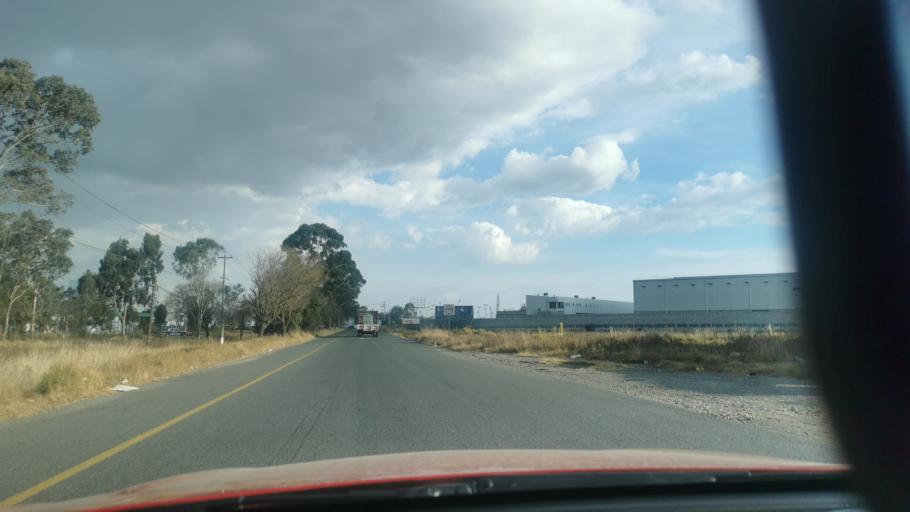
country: MX
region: Mexico
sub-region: Toluca
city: Colonia Aviacion Autopan
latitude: 19.3838
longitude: -99.7079
